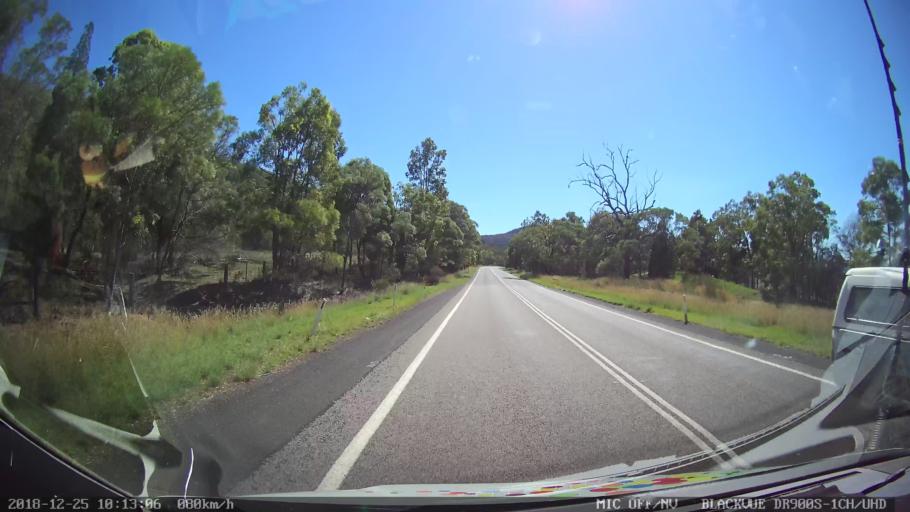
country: AU
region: New South Wales
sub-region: Muswellbrook
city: Denman
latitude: -32.3260
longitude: 150.5401
